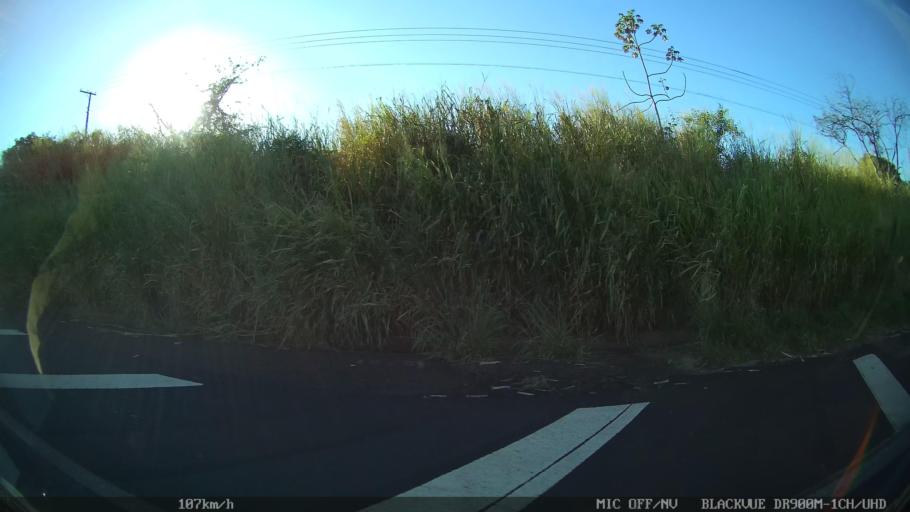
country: BR
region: Sao Paulo
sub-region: Olimpia
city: Olimpia
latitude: -20.7285
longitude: -49.0474
